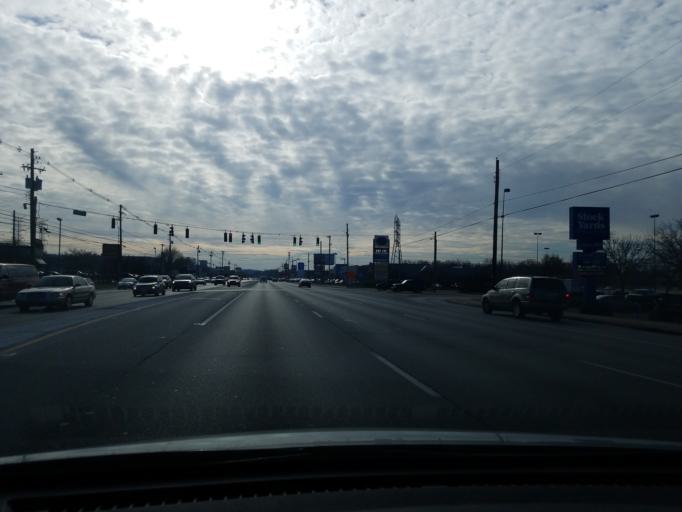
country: US
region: Kentucky
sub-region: Jefferson County
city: Saint Dennis
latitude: 38.1626
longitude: -85.8315
